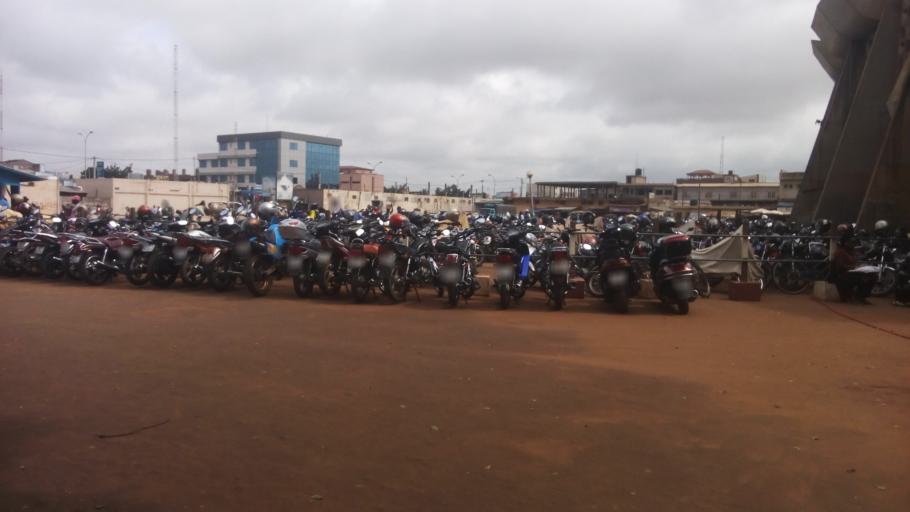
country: TG
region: Maritime
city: Lome
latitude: 6.1816
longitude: 1.2412
